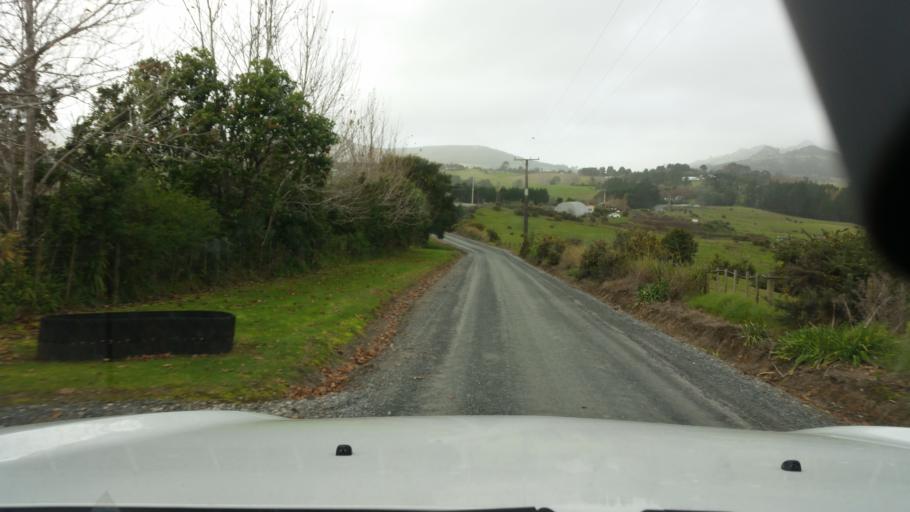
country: NZ
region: Northland
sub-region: Whangarei
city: Ngunguru
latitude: -35.7547
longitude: 174.4913
